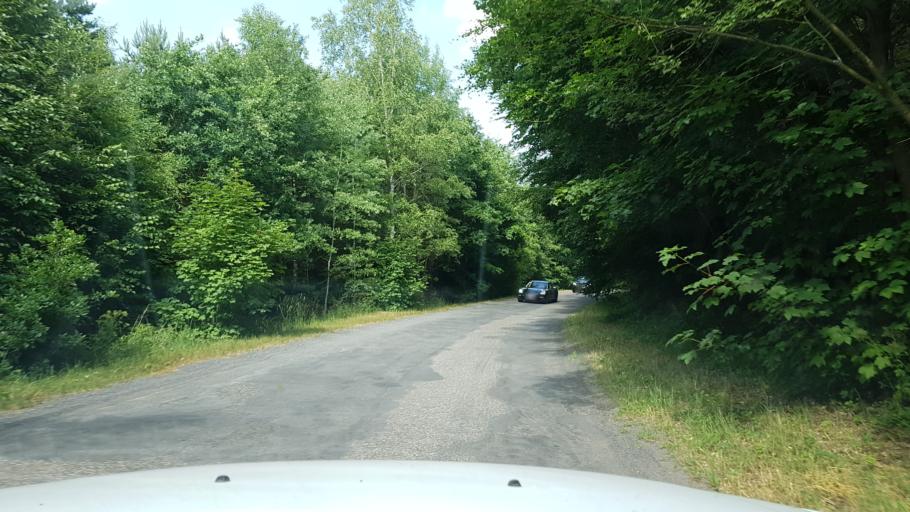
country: PL
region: West Pomeranian Voivodeship
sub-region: Powiat goleniowski
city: Mosty
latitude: 53.5548
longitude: 14.9663
